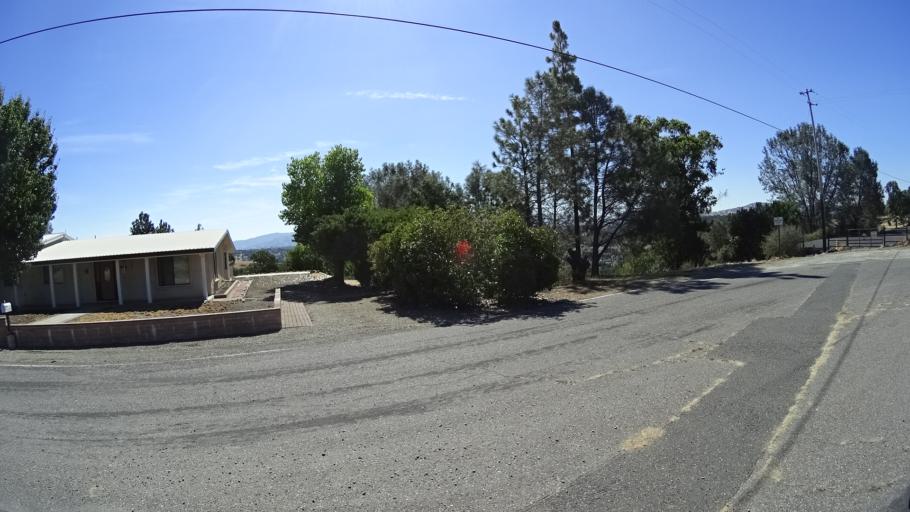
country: US
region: California
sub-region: Calaveras County
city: Rancho Calaveras
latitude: 38.1602
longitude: -120.8594
